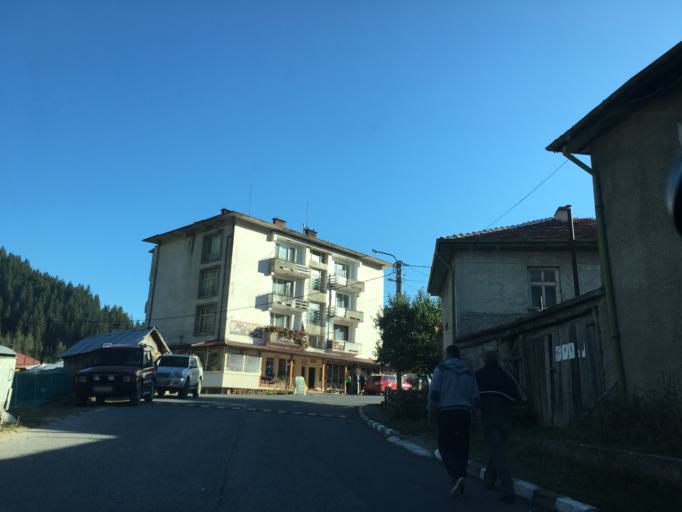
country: BG
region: Smolyan
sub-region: Obshtina Borino
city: Borino
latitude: 41.5995
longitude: 24.3796
